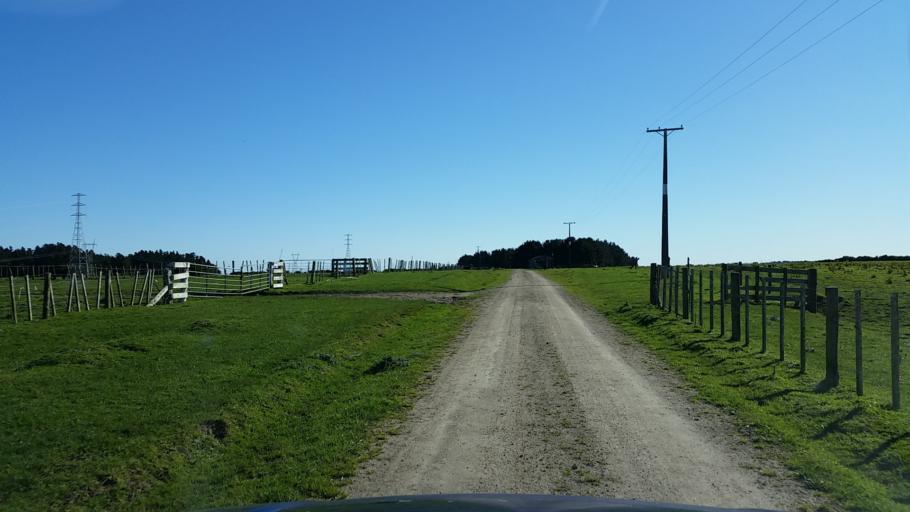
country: NZ
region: Taranaki
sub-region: South Taranaki District
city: Patea
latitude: -39.7893
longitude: 174.7593
